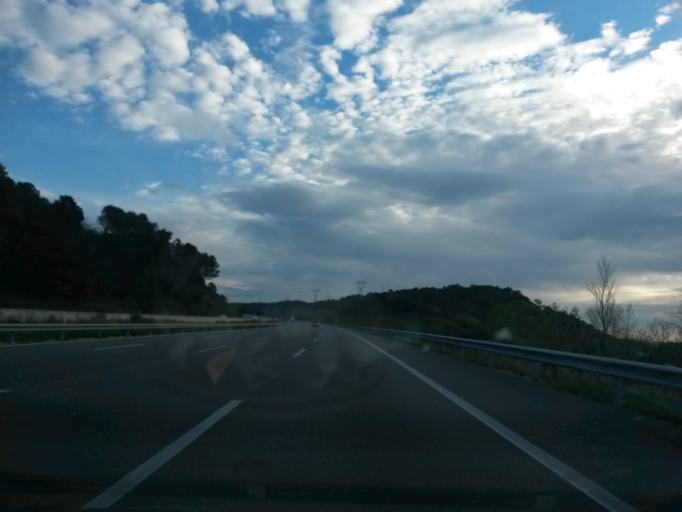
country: ES
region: Catalonia
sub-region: Provincia de Girona
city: Celra
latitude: 42.0561
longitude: 2.8818
